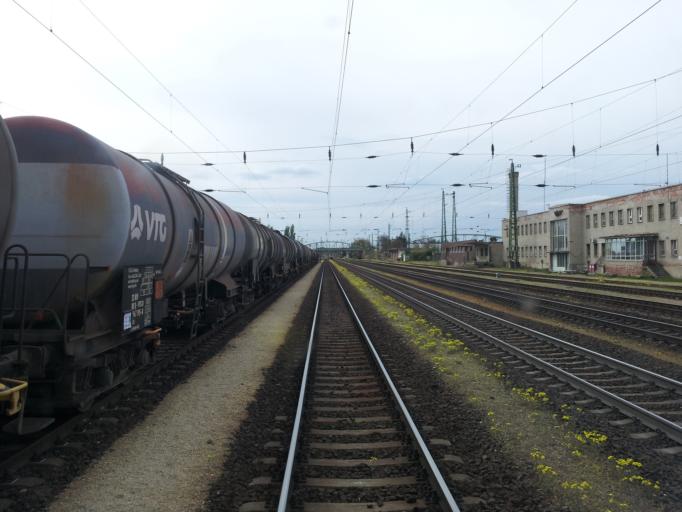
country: HU
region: Komarom-Esztergom
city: Komarom
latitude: 47.7481
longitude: 18.1264
